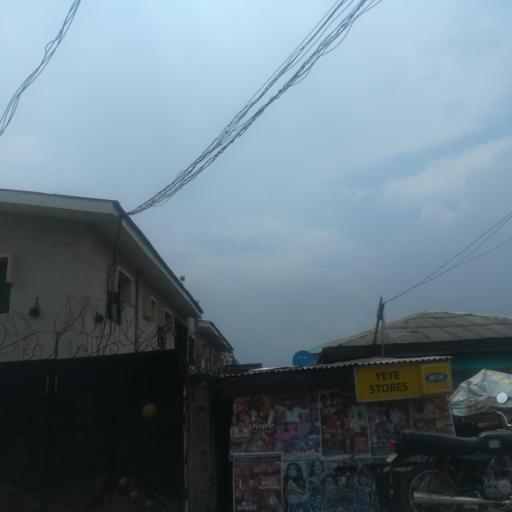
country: NG
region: Lagos
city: Ojota
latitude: 6.5778
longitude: 3.4014
